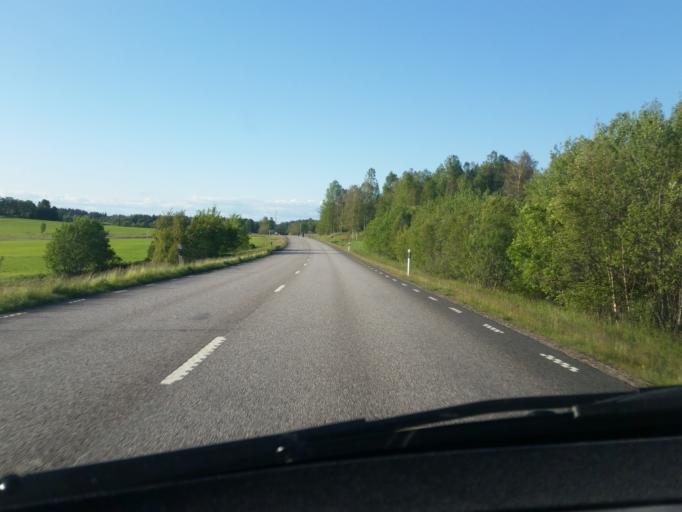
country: SE
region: Vaestra Goetaland
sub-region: Fargelanda Kommun
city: Faergelanda
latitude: 58.5394
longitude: 11.9870
